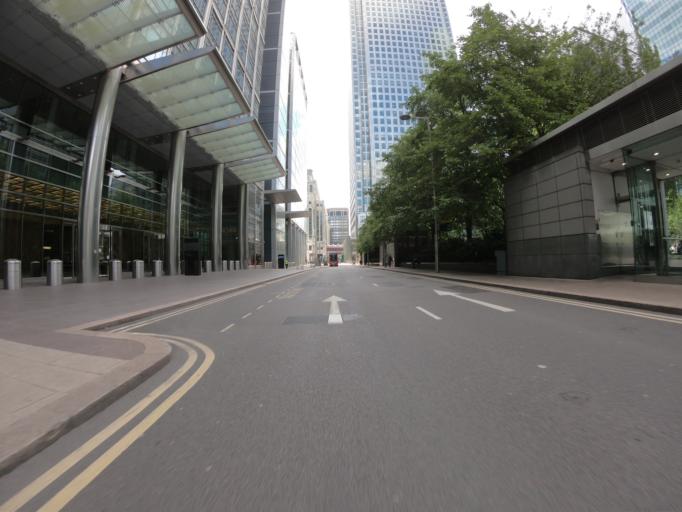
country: GB
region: England
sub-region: Greater London
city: Poplar
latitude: 51.5043
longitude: -0.0174
